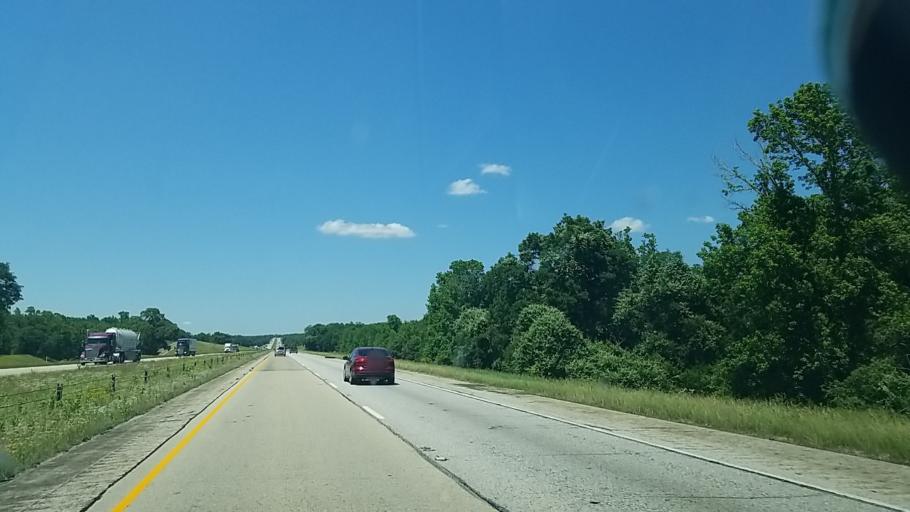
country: US
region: Texas
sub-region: Leon County
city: Centerville
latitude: 31.1731
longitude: -95.9883
